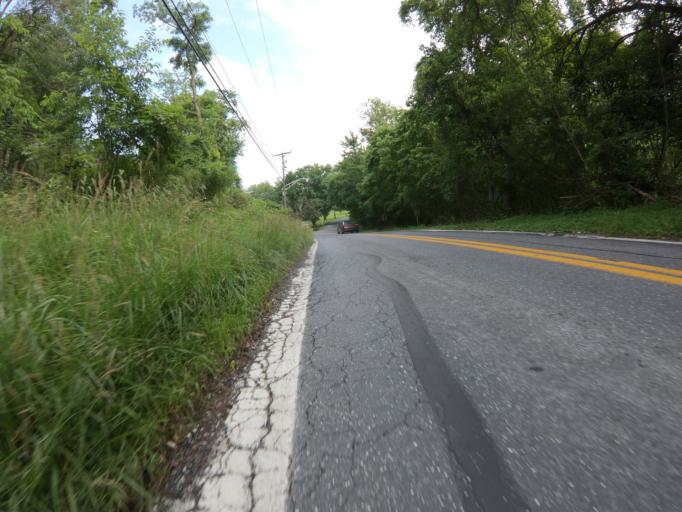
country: US
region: Maryland
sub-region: Howard County
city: Ellicott City
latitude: 39.2581
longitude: -76.7910
